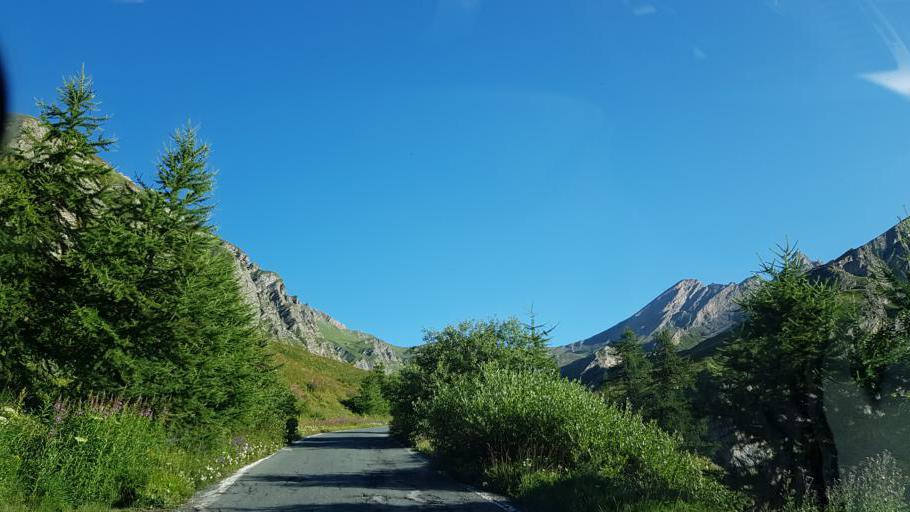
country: IT
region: Piedmont
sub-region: Provincia di Cuneo
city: Pontechianale
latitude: 44.6582
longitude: 6.9862
